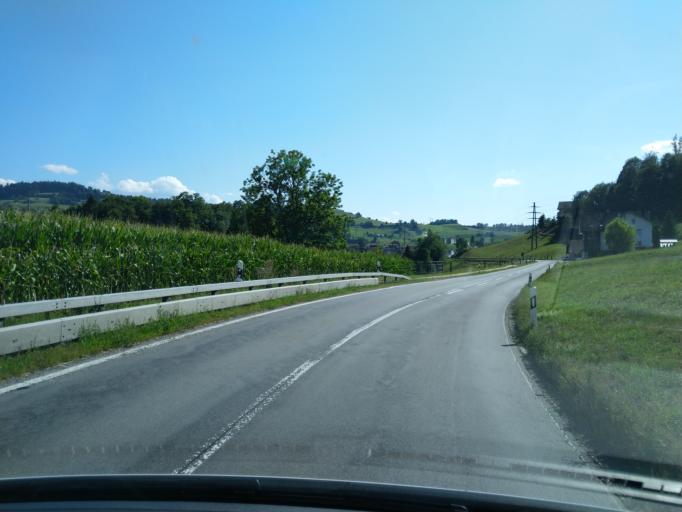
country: CH
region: Lucerne
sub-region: Entlebuch District
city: Werthenstein
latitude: 47.0632
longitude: 8.0971
